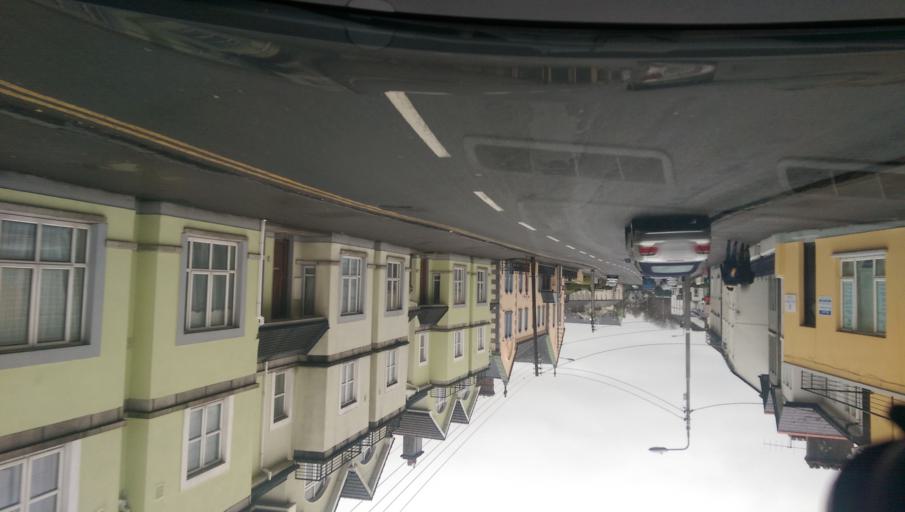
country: IE
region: Connaught
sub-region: County Galway
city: Gaillimh
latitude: 53.2667
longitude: -9.0700
